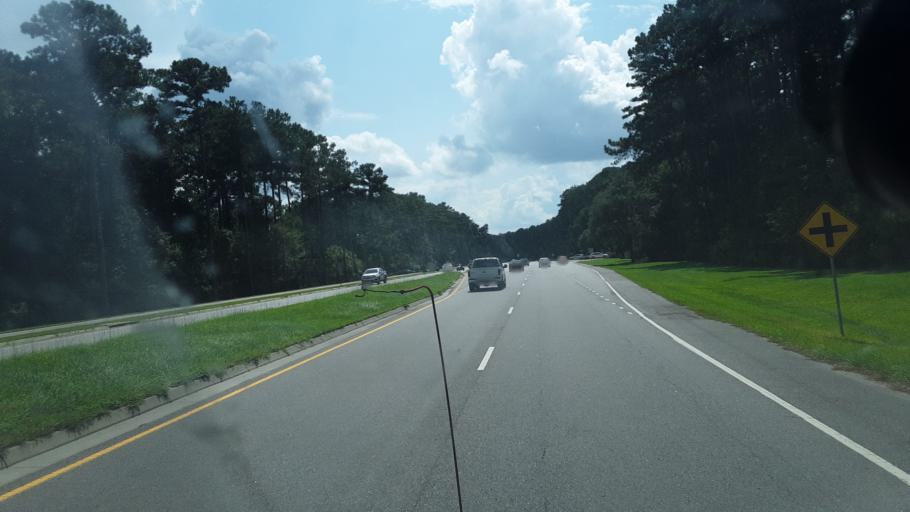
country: US
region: South Carolina
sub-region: Beaufort County
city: Bluffton
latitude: 32.2877
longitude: -80.9411
